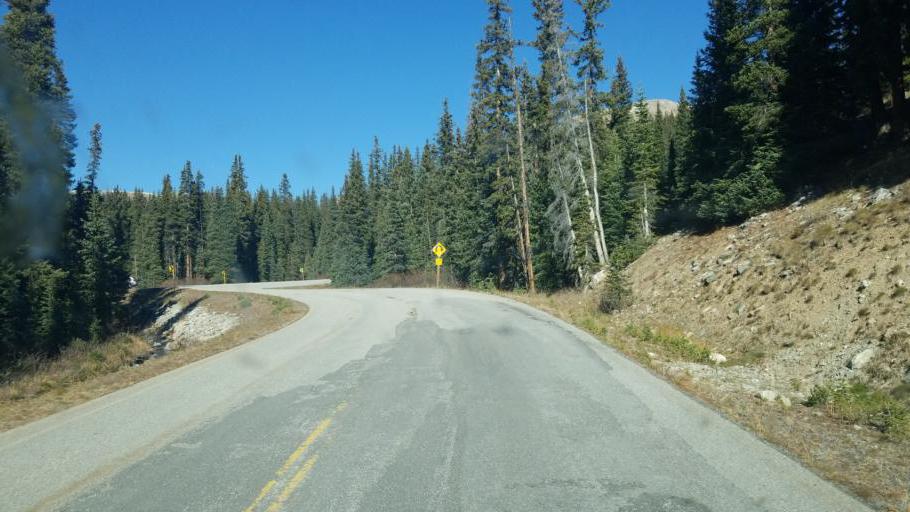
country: US
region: Colorado
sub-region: Chaffee County
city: Buena Vista
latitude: 38.8075
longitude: -106.3899
